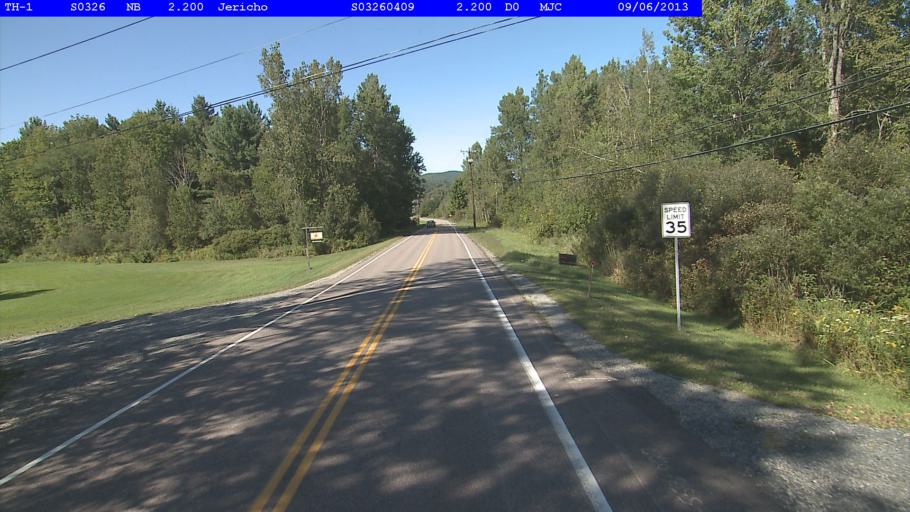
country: US
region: Vermont
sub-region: Chittenden County
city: Jericho
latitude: 44.5082
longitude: -72.9540
